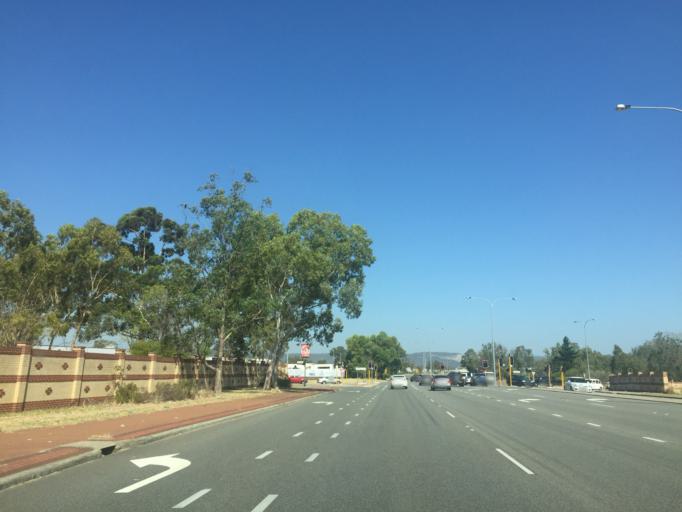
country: AU
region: Western Australia
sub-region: Gosnells
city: Kenwick
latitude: -32.0409
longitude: 115.9660
